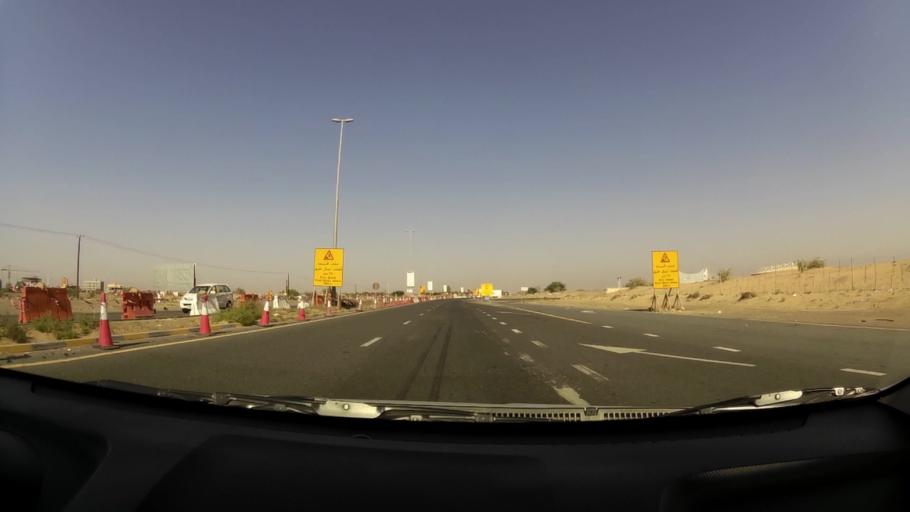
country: AE
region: Umm al Qaywayn
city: Umm al Qaywayn
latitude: 25.4702
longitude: 55.5843
